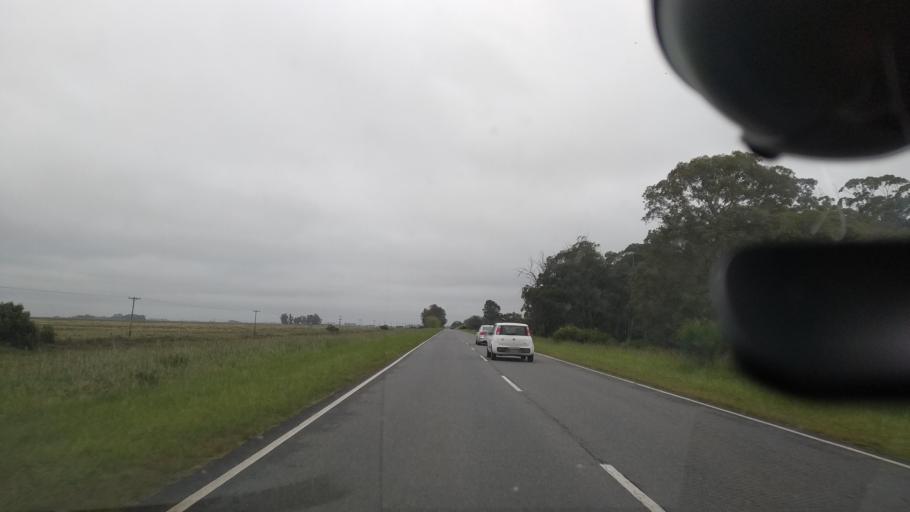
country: AR
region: Buenos Aires
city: Veronica
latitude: -35.4639
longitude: -57.3265
